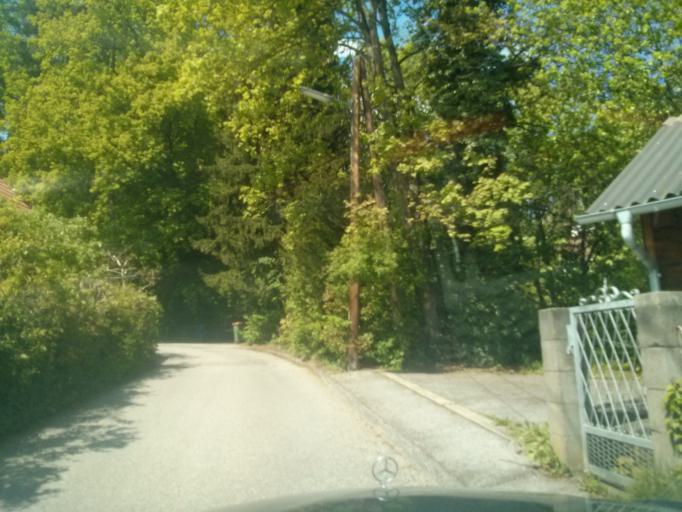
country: AT
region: Styria
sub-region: Politischer Bezirk Graz-Umgebung
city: Stattegg
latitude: 47.1199
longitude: 15.4203
